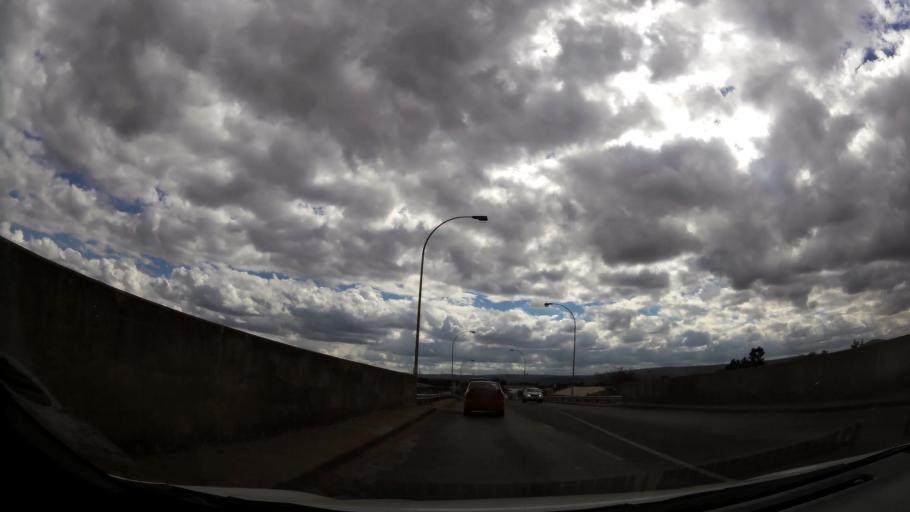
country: ZA
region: Limpopo
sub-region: Waterberg District Municipality
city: Modimolle
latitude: -24.7134
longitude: 28.4180
